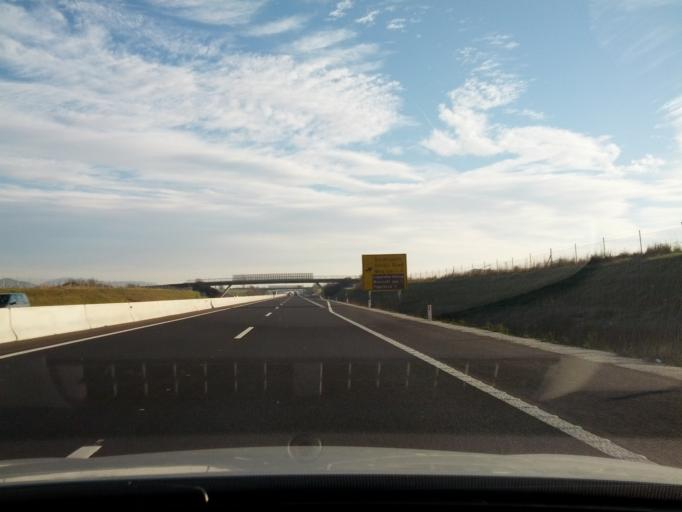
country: SI
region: Polzela
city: Polzela
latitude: 46.2589
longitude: 15.0644
